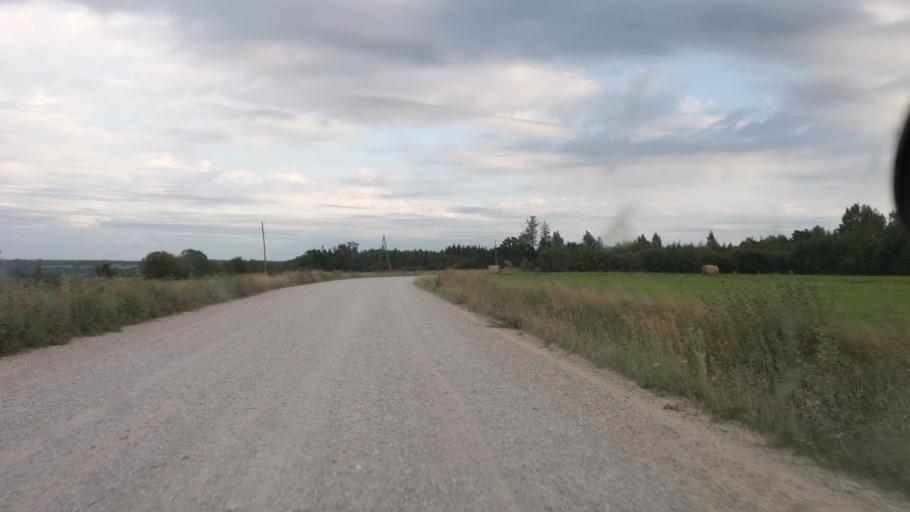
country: LV
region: Talsu Rajons
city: Sabile
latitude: 57.0254
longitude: 22.5846
